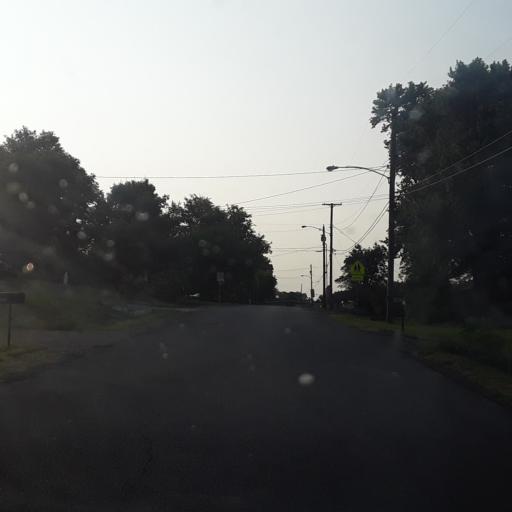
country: US
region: Tennessee
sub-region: Williamson County
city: Brentwood
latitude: 36.0602
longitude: -86.7252
